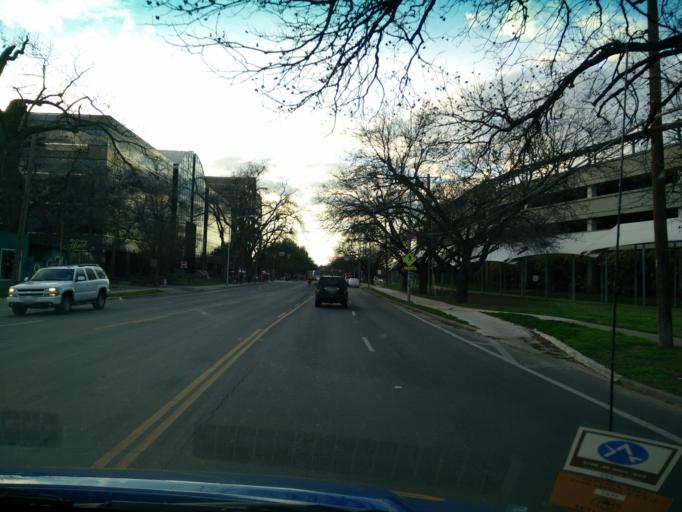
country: US
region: Texas
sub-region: Travis County
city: Austin
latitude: 30.2587
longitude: -97.7508
